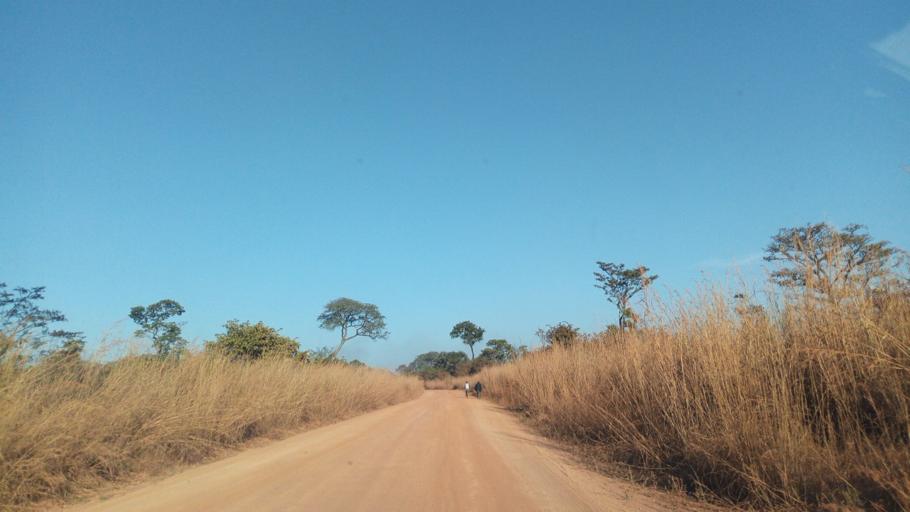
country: ZM
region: Luapula
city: Mwense
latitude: -10.4843
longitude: 28.5005
